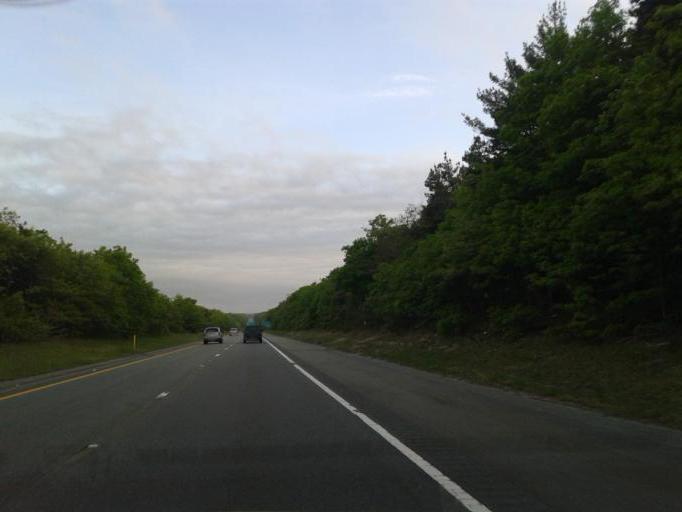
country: US
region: Massachusetts
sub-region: Barnstable County
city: North Falmouth
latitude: 41.6359
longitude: -70.6092
